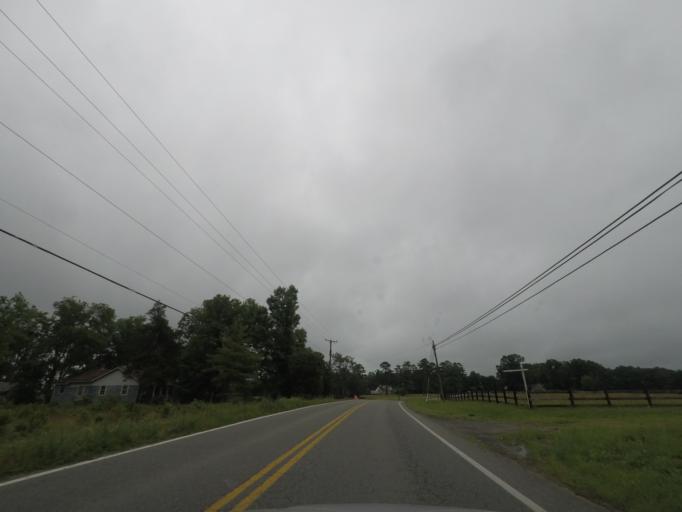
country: US
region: Virginia
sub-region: Fluvanna County
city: Weber City
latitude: 37.7752
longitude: -78.2506
